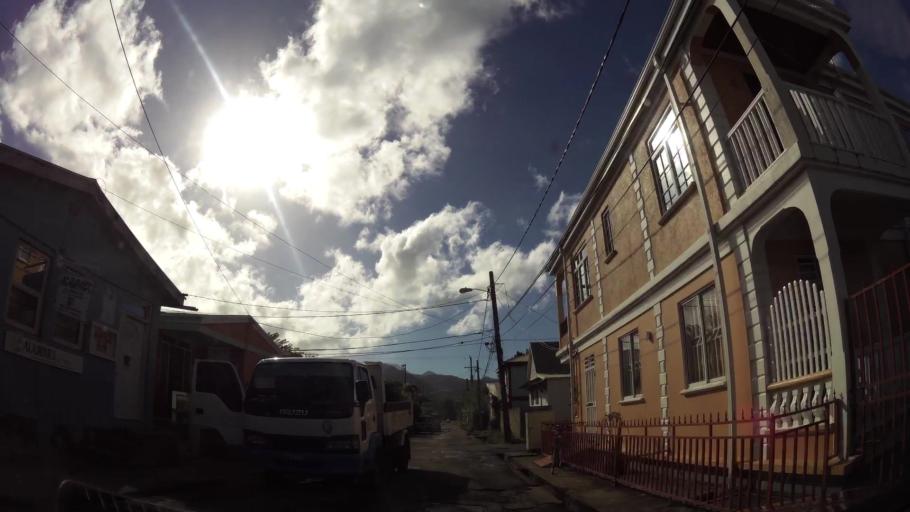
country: DM
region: Saint John
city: Portsmouth
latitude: 15.5765
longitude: -61.4560
